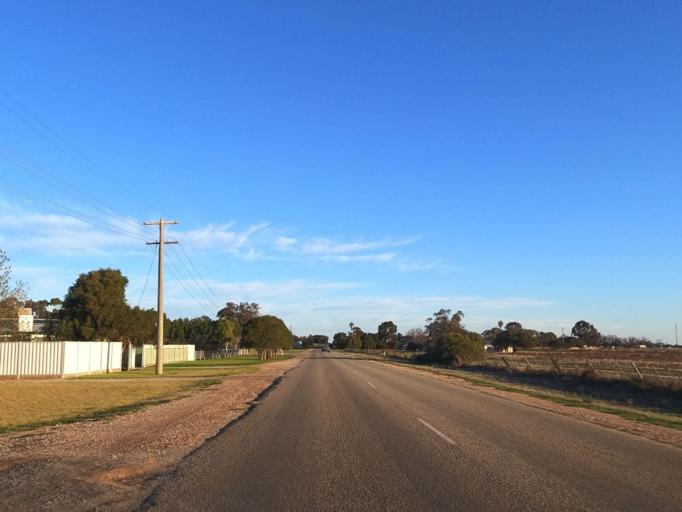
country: AU
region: Victoria
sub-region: Swan Hill
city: Swan Hill
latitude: -35.3570
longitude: 143.5523
